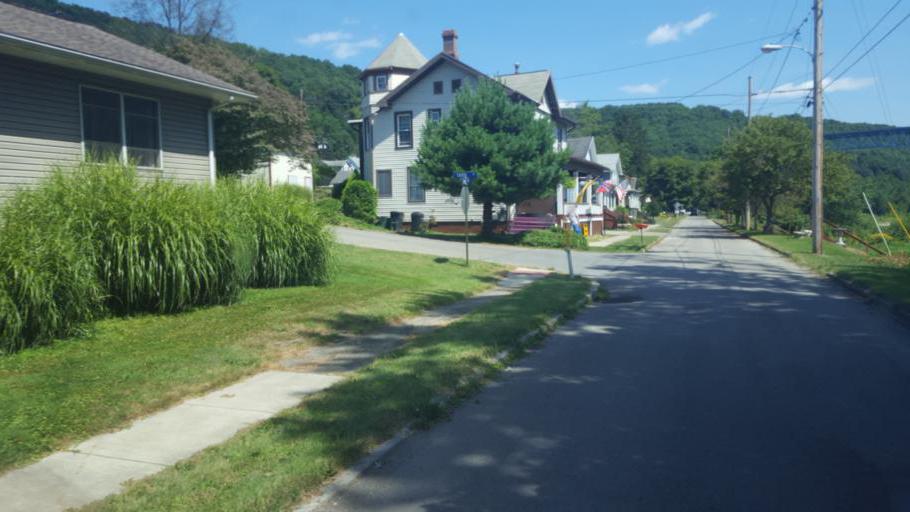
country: US
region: Pennsylvania
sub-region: Clarion County
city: Knox
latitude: 41.1765
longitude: -79.7056
